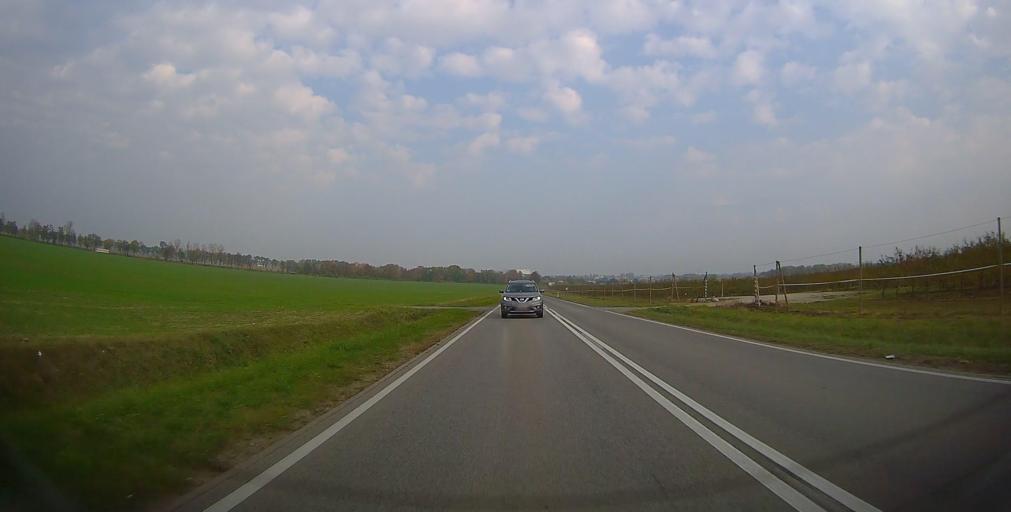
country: PL
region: Masovian Voivodeship
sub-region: Powiat grojecki
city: Belsk Duzy
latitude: 51.8033
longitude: 20.7905
